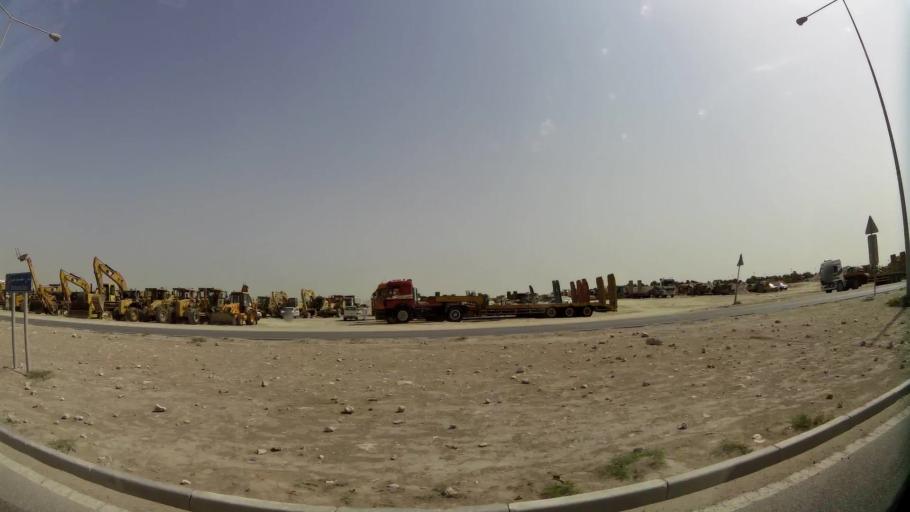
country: QA
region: Al Wakrah
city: Al Wukayr
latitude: 25.1757
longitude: 51.4671
